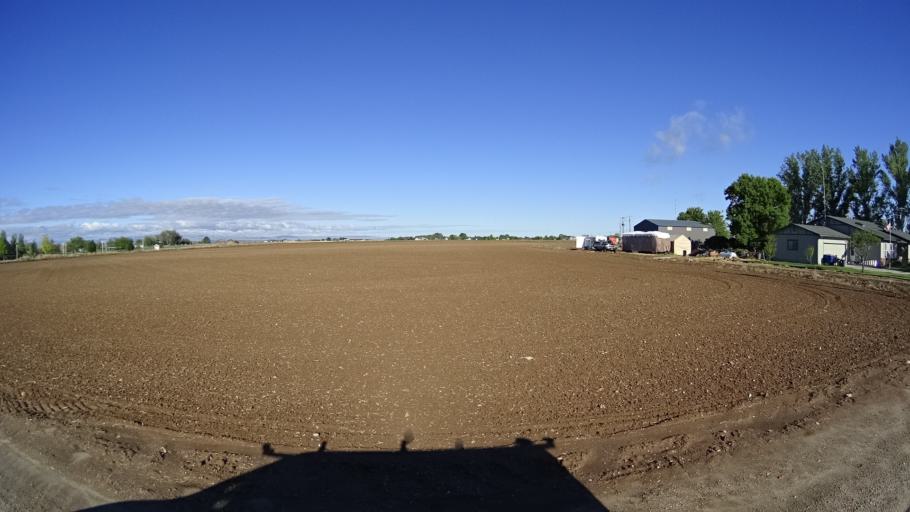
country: US
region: Idaho
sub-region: Ada County
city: Kuna
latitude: 43.5278
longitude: -116.4138
